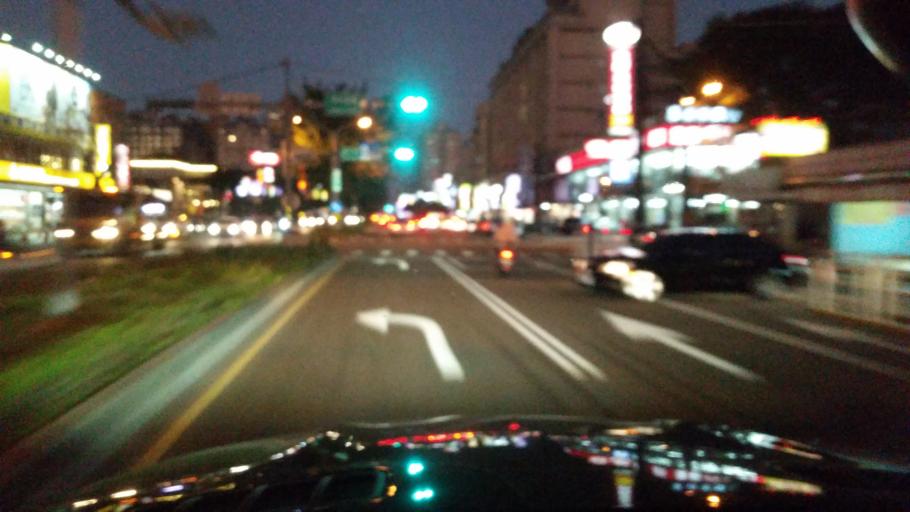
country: TW
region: Taiwan
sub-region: Taoyuan
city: Taoyuan
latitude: 25.0553
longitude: 121.3616
